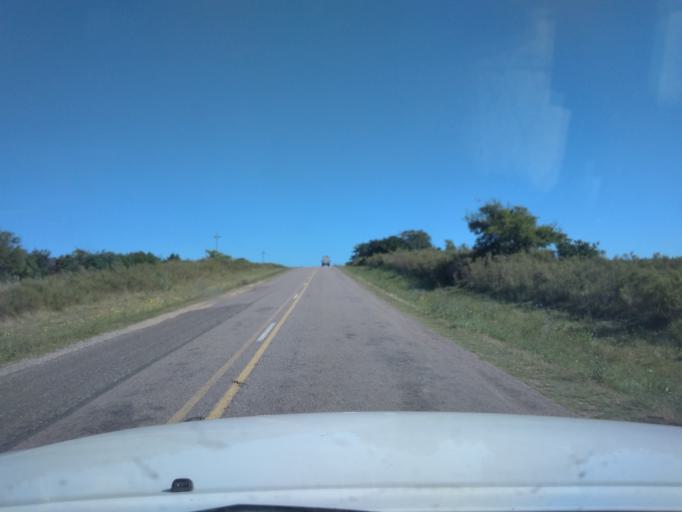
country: UY
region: Canelones
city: San Ramon
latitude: -34.1801
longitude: -55.9418
